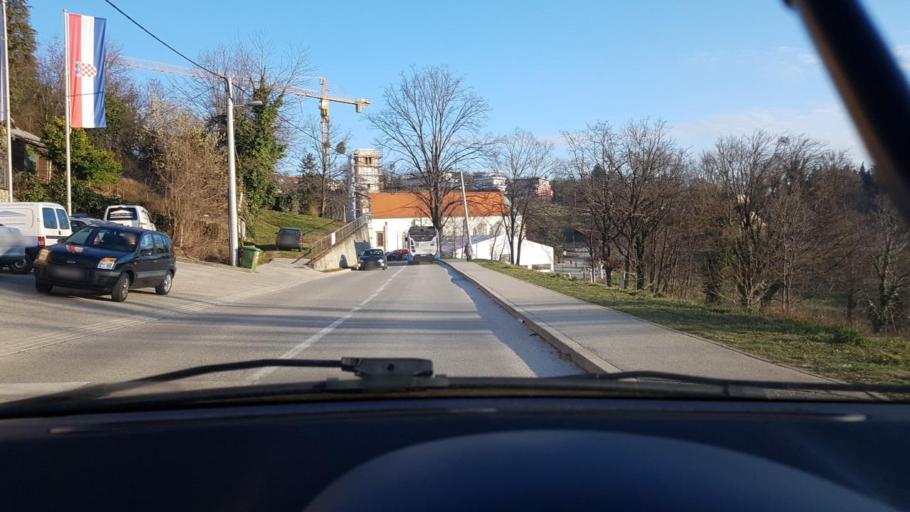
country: HR
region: Grad Zagreb
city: Zagreb
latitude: 45.8496
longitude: 15.9900
